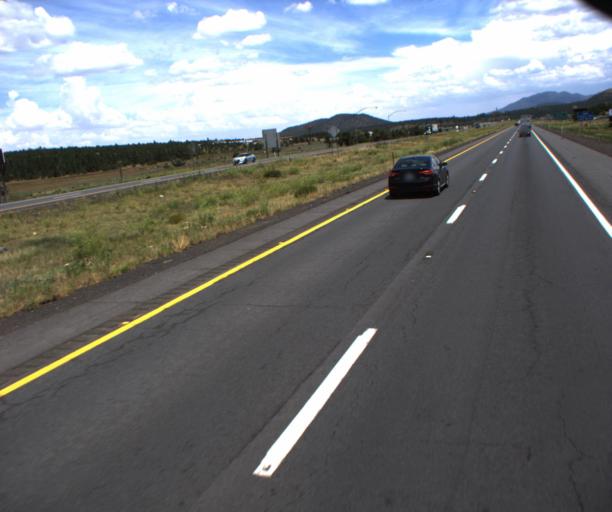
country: US
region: Arizona
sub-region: Coconino County
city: Williams
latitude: 35.2546
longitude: -112.2015
